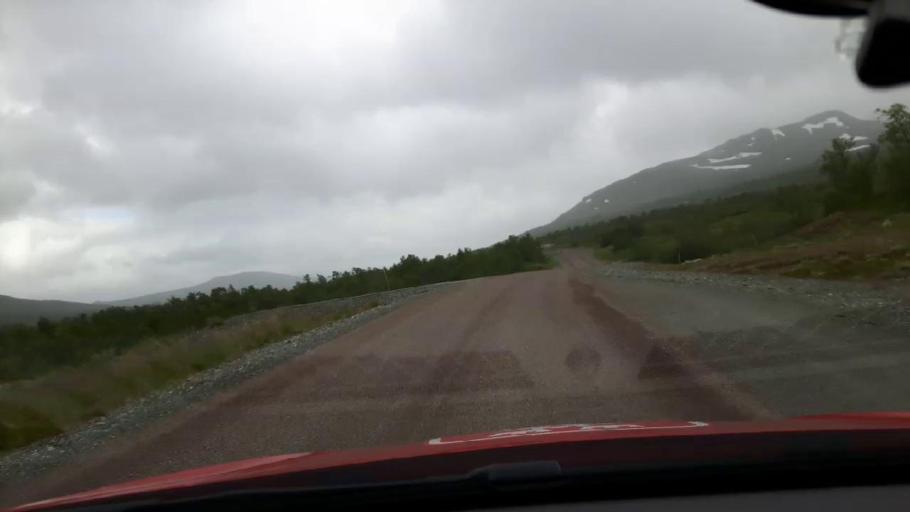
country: NO
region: Nord-Trondelag
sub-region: Meraker
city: Meraker
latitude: 63.2035
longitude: 12.3950
